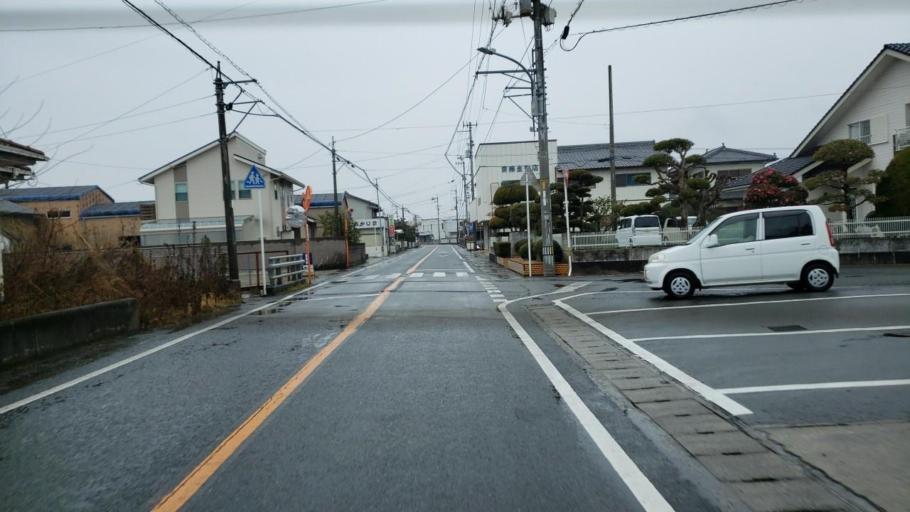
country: JP
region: Tokushima
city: Kamojimacho-jogejima
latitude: 34.0995
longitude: 134.3855
